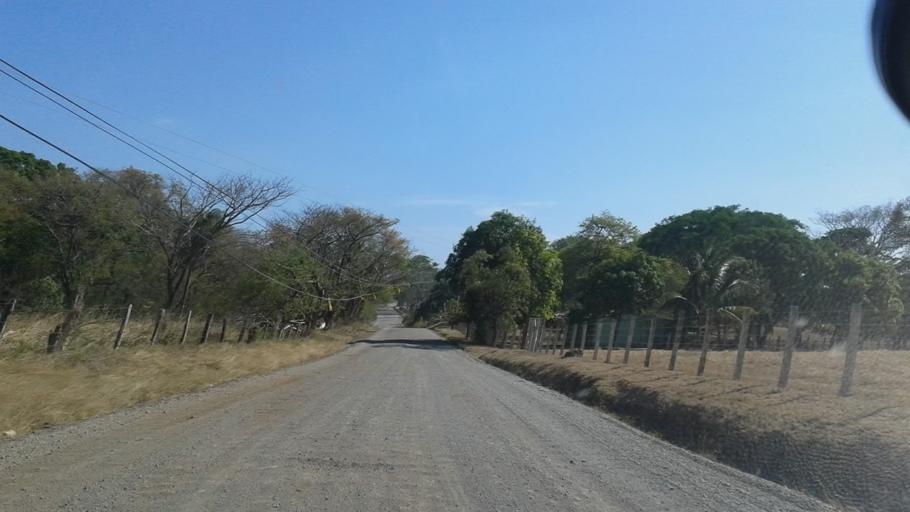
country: CR
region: Guanacaste
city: Santa Cruz
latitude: 10.1345
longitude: -85.7894
